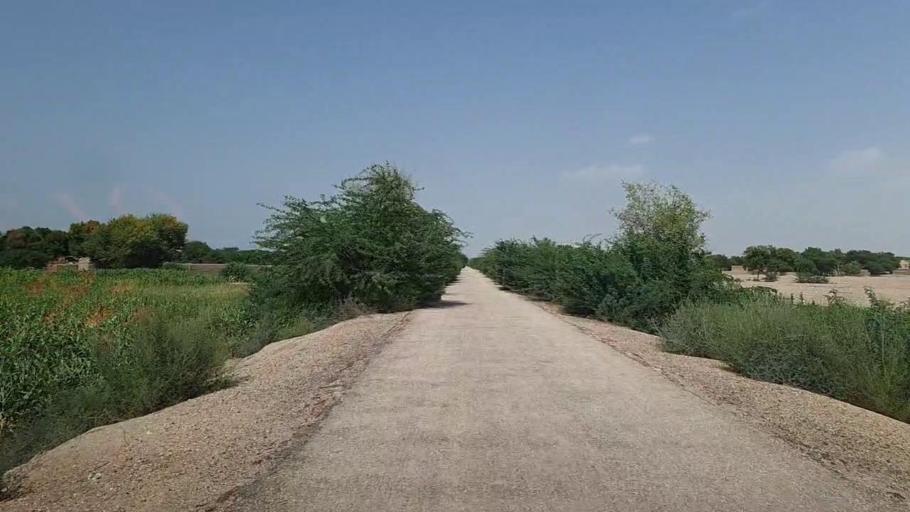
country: PK
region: Sindh
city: Pad Idan
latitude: 26.7883
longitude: 68.3496
